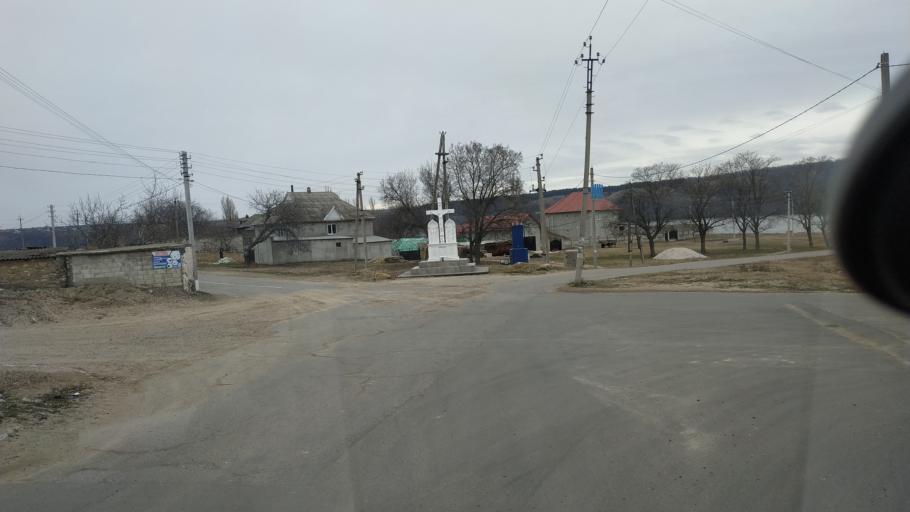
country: MD
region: Telenesti
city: Cocieri
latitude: 47.3416
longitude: 29.1186
